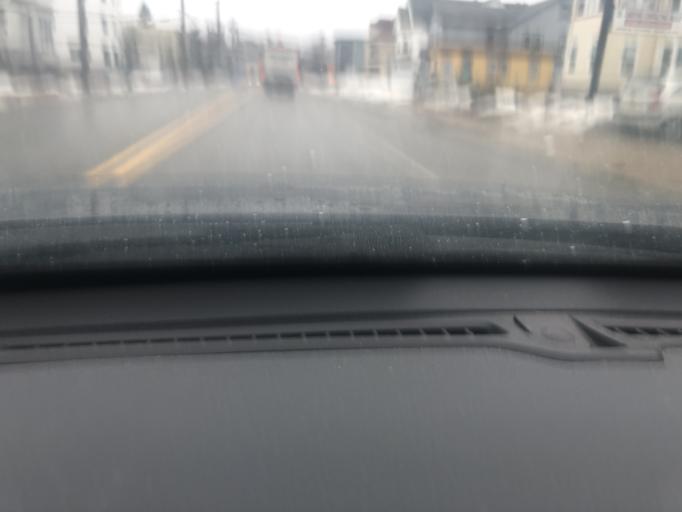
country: US
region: Massachusetts
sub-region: Plymouth County
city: Brockton
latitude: 42.1022
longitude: -71.0223
